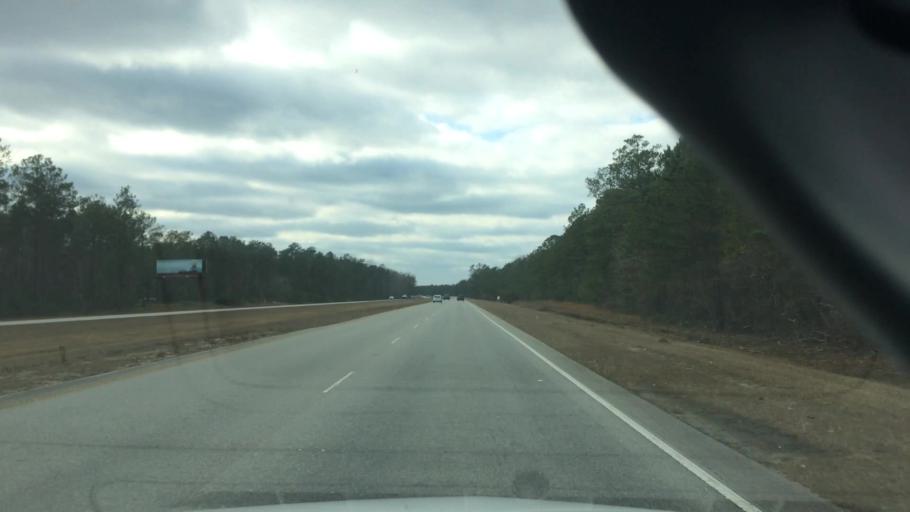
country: US
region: North Carolina
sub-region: Brunswick County
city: Bolivia
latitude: 34.0775
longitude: -78.1474
